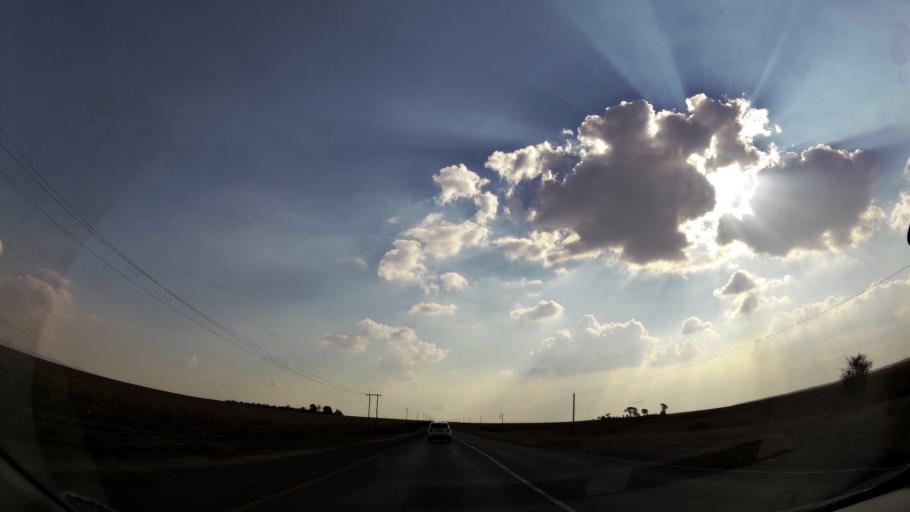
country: ZA
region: Gauteng
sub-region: Sedibeng District Municipality
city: Heidelberg
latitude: -26.3885
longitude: 28.3431
